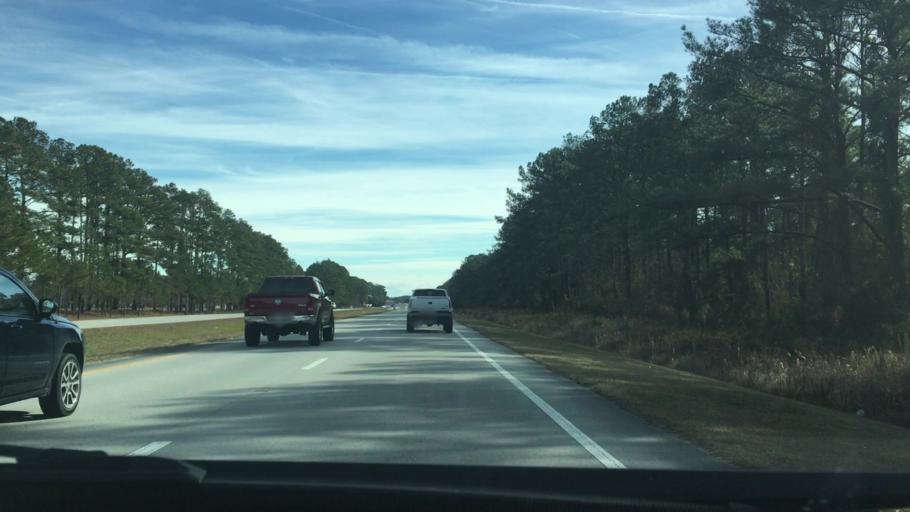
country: US
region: North Carolina
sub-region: Carteret County
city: Newport
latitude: 34.7650
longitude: -76.8585
